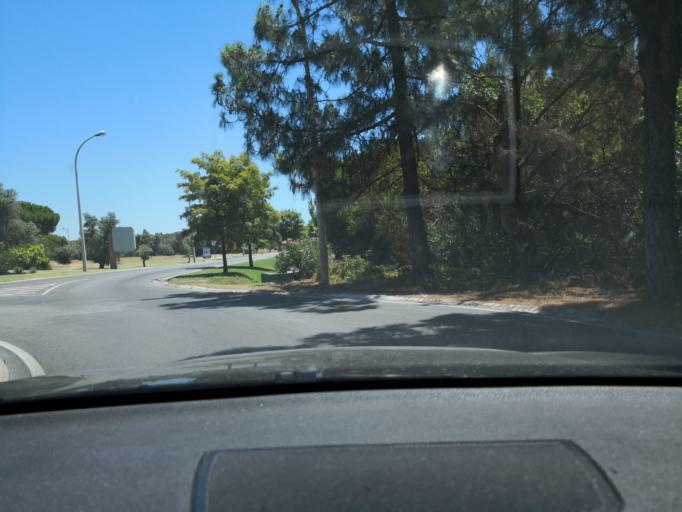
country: PT
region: Faro
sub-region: Loule
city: Vilamoura
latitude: 37.1051
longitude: -8.1301
